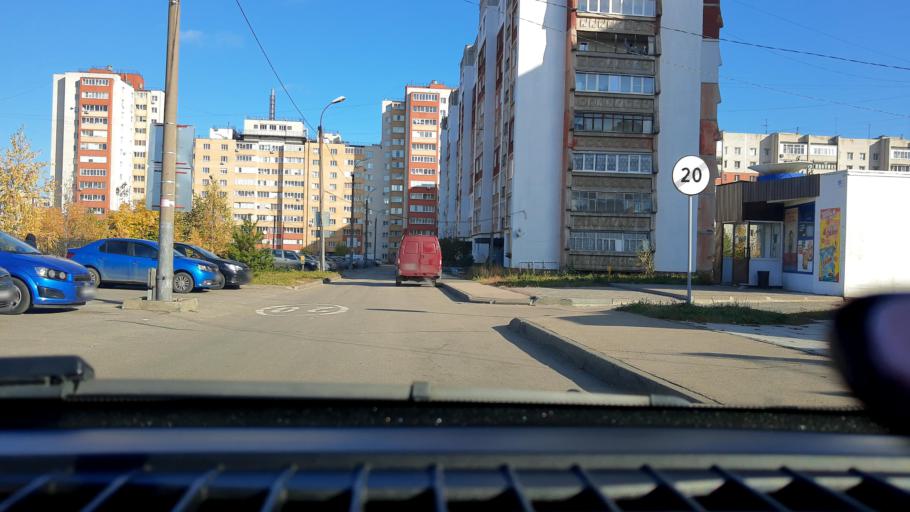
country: RU
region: Nizjnij Novgorod
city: Kstovo
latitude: 56.1583
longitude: 44.2139
